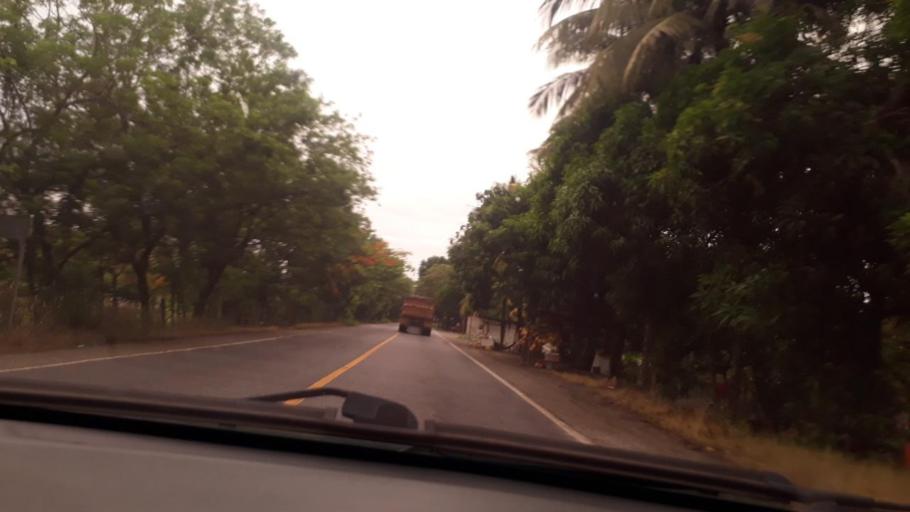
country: GT
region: Izabal
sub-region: Municipio de Los Amates
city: Los Amates
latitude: 15.3197
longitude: -89.0466
